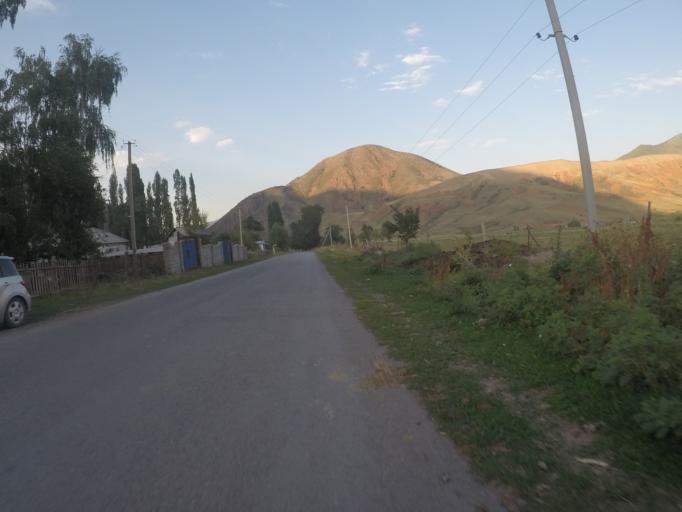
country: KG
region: Chuy
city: Bishkek
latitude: 42.6727
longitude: 74.6504
